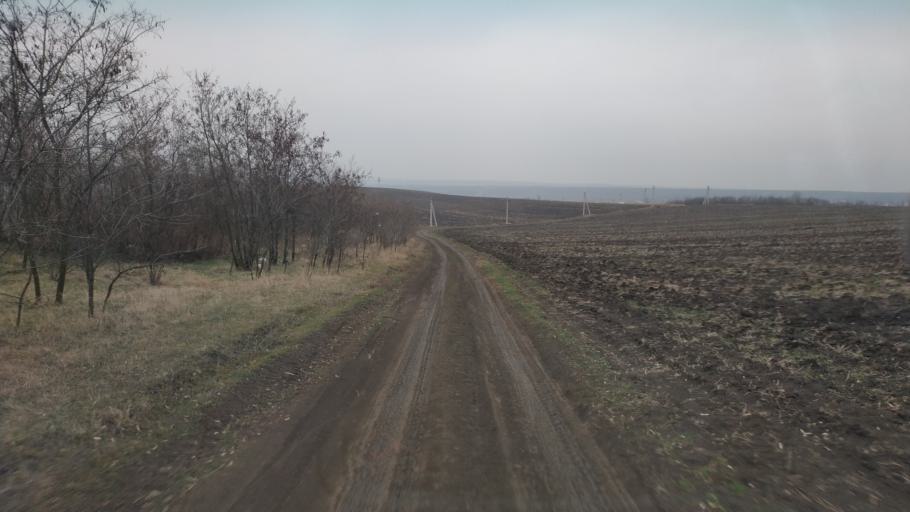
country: MD
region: Chisinau
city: Singera
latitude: 46.8233
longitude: 28.9836
